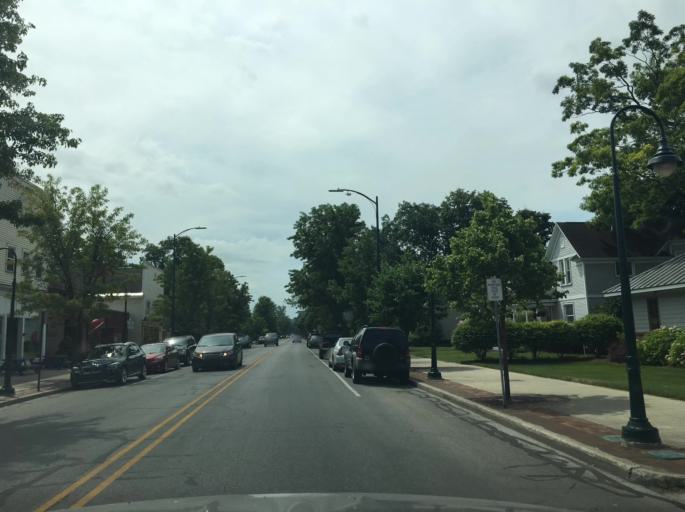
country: US
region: Michigan
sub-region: Grand Traverse County
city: Traverse City
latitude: 44.7591
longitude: -85.6239
